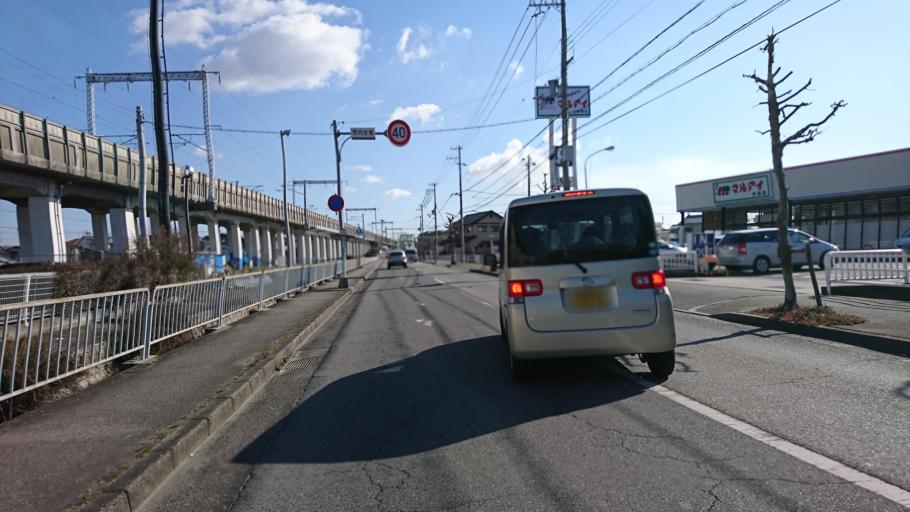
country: JP
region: Hyogo
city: Kakogawacho-honmachi
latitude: 34.7727
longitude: 134.7915
